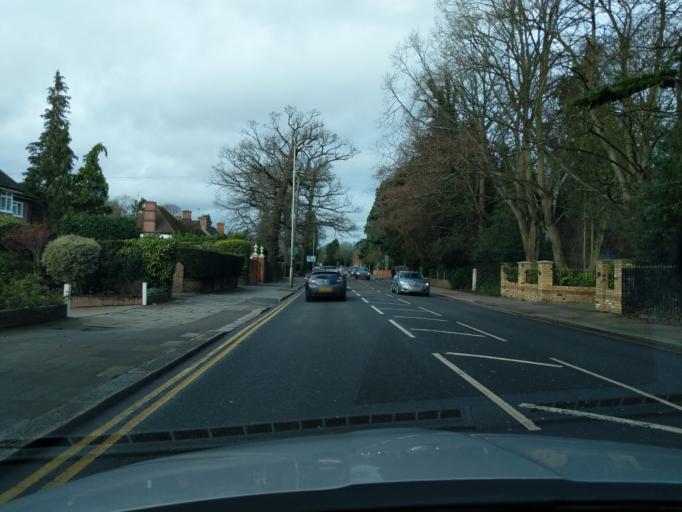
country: GB
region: England
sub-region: Hertfordshire
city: Watford
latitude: 51.6673
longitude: -0.4116
